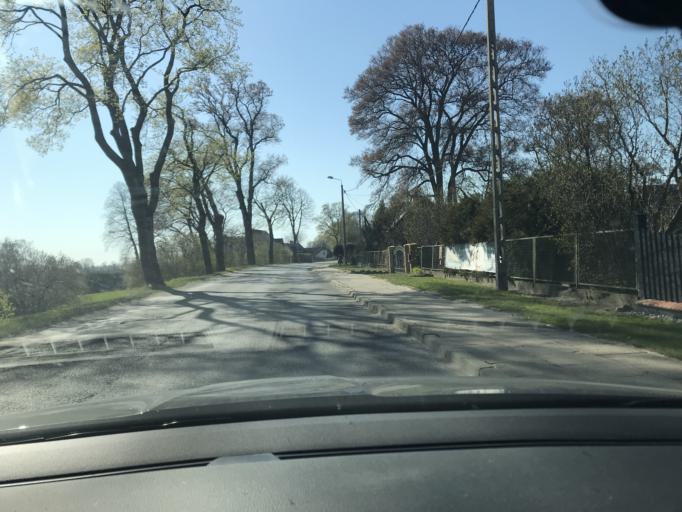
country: PL
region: Pomeranian Voivodeship
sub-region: Powiat nowodworski
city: Sztutowo
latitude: 54.3265
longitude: 19.1637
